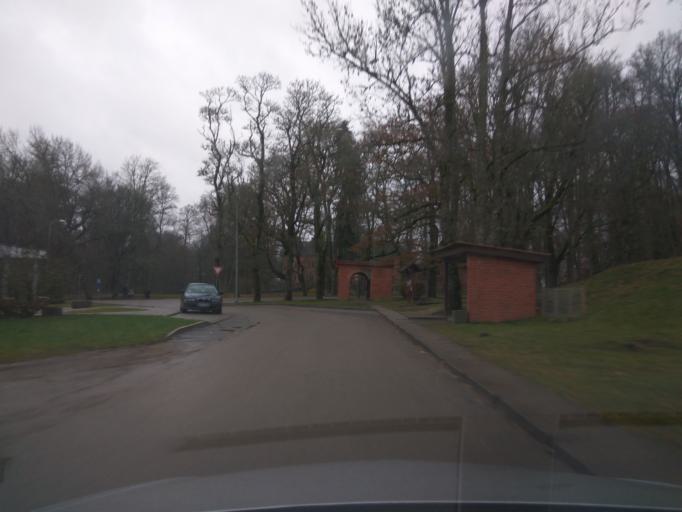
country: LV
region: Kuldigas Rajons
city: Kuldiga
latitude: 56.9205
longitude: 21.9675
